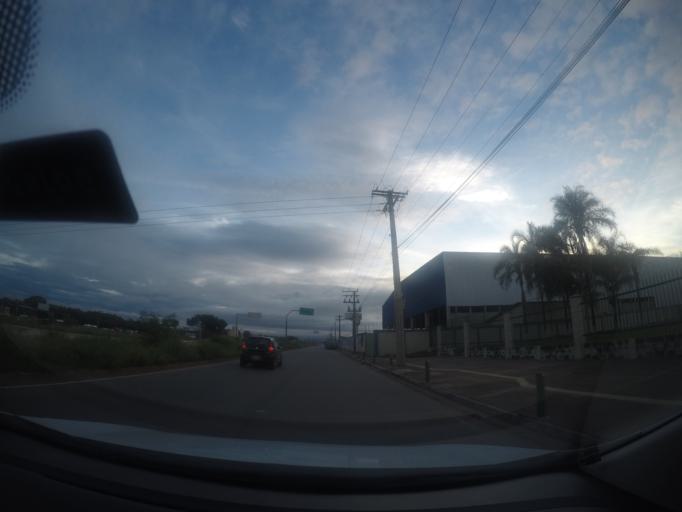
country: BR
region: Goias
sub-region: Goiania
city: Goiania
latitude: -16.7167
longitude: -49.3642
